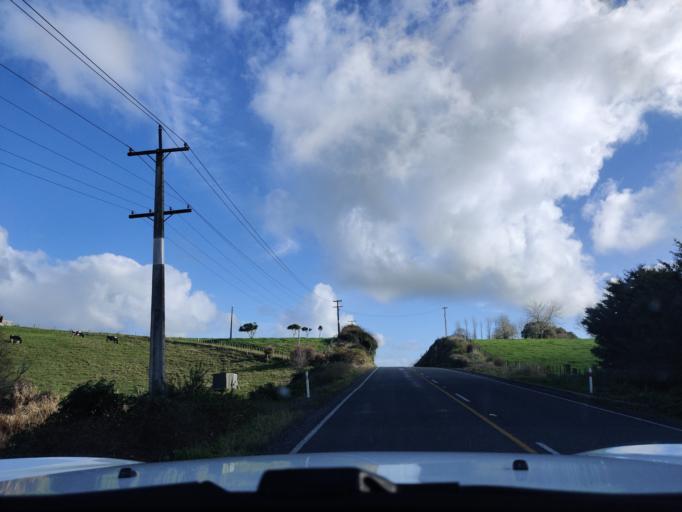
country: NZ
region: Waikato
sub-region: Waikato District
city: Te Kauwhata
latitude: -37.3695
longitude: 175.2423
